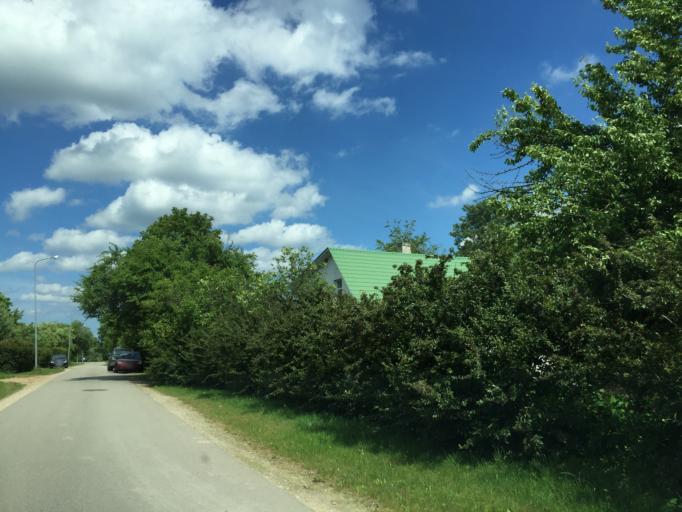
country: LV
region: Engure
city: Smarde
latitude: 56.9566
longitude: 23.3330
